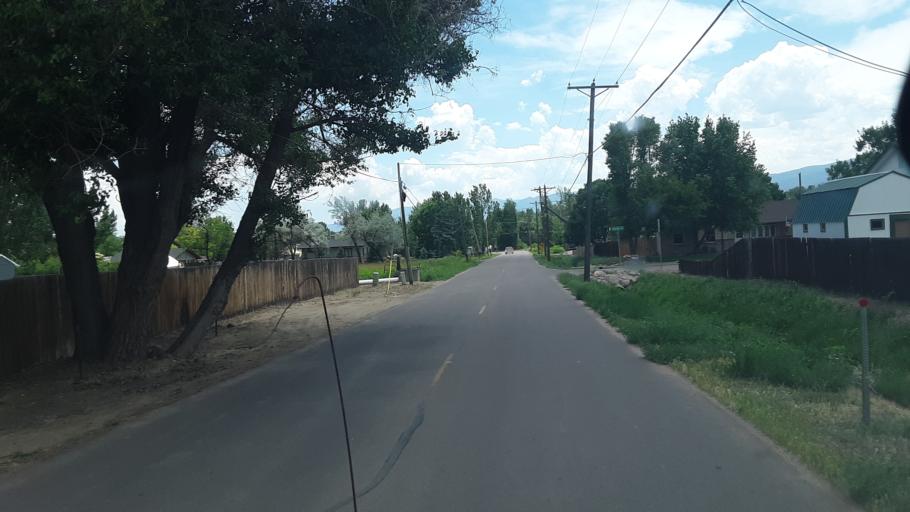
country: US
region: Colorado
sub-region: Fremont County
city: Lincoln Park
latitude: 38.4440
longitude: -105.2040
